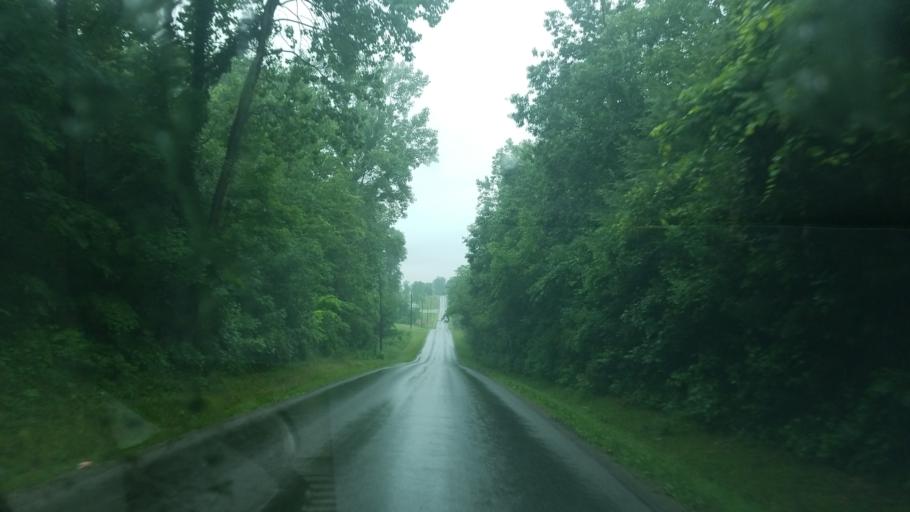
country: US
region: Ohio
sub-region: Huron County
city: Greenwich
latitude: 40.9385
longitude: -82.5553
